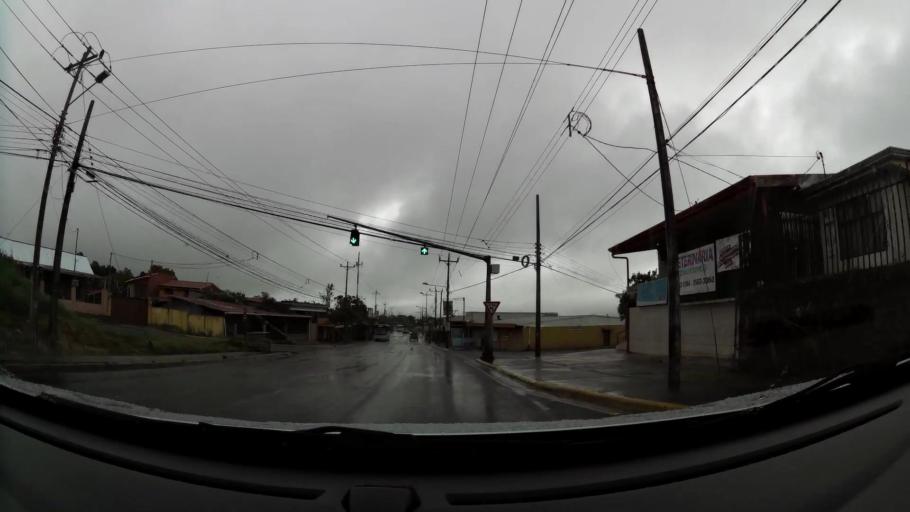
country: CR
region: Cartago
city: Cartago
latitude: 9.8548
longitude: -83.9036
